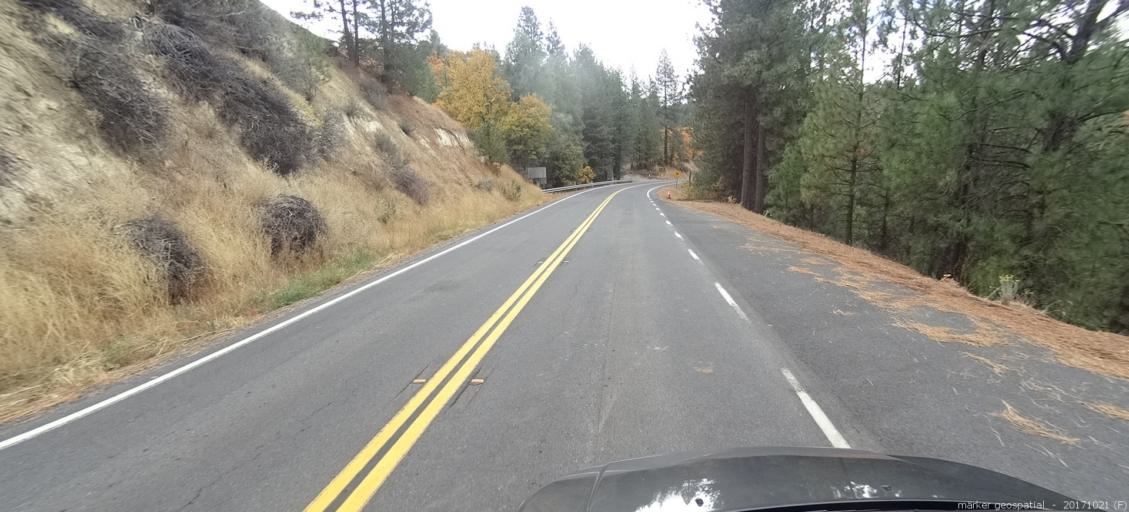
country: US
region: California
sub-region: Shasta County
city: Burney
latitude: 41.0212
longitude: -121.6219
